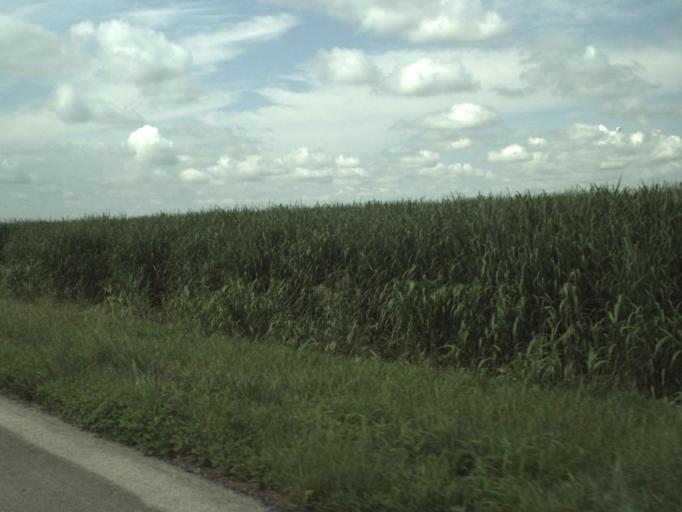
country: US
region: Florida
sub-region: Palm Beach County
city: Belle Glade Camp
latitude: 26.6698
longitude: -80.6869
